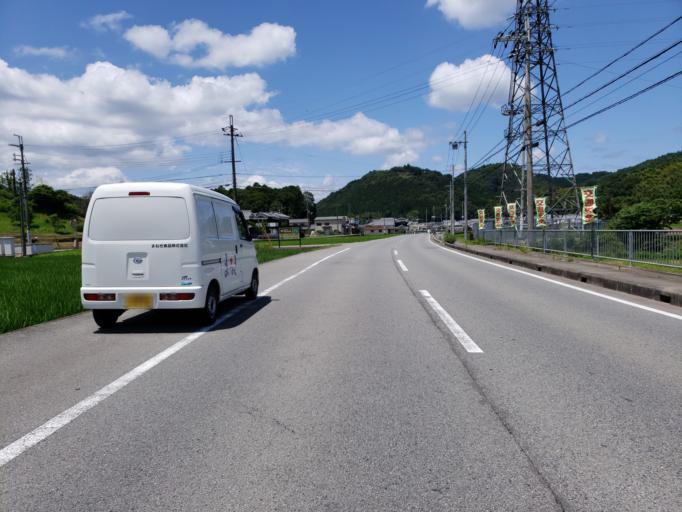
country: JP
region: Hyogo
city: Himeji
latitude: 34.9375
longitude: 134.7209
